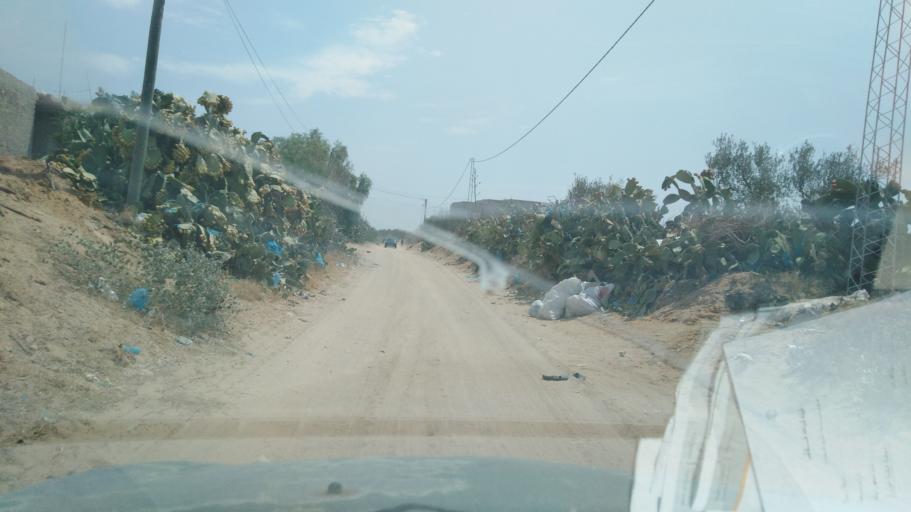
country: TN
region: Safaqis
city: Sfax
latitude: 34.7395
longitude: 10.5413
